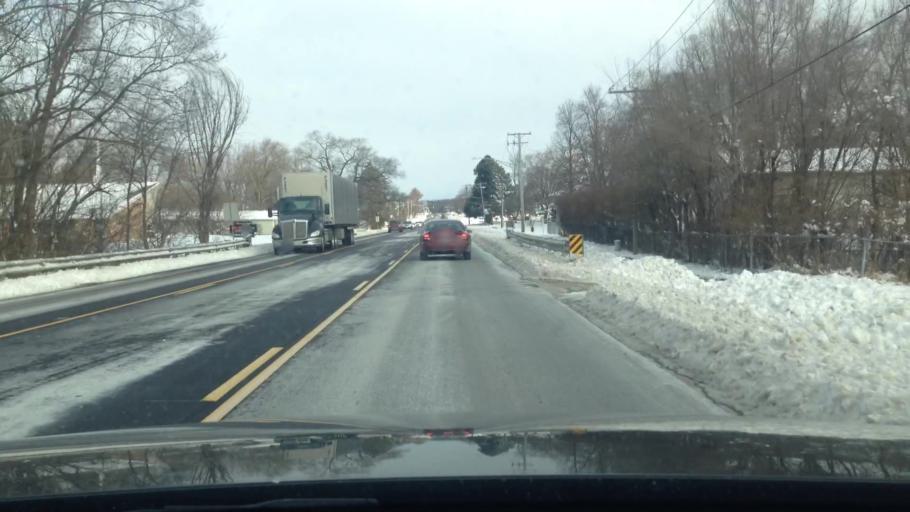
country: US
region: Illinois
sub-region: McHenry County
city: Woodstock
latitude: 42.3348
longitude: -88.4432
